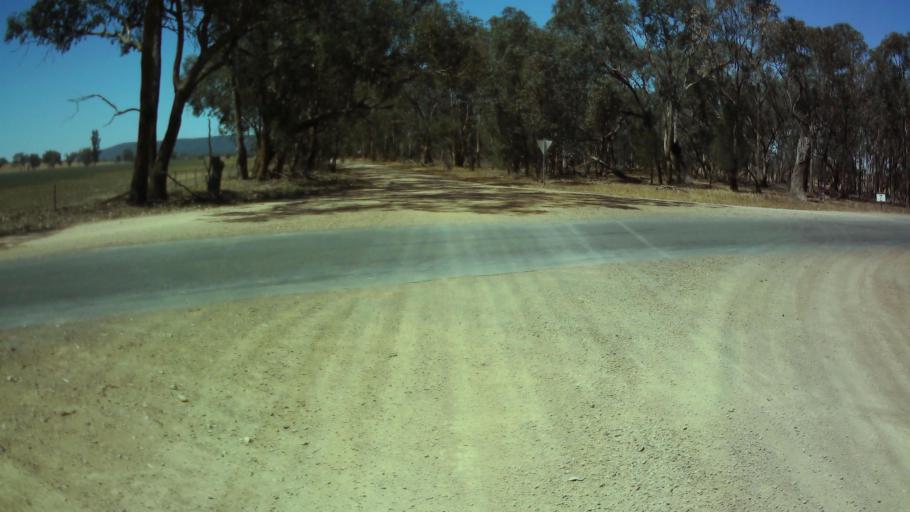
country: AU
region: New South Wales
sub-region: Weddin
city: Grenfell
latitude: -33.9074
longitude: 148.0804
